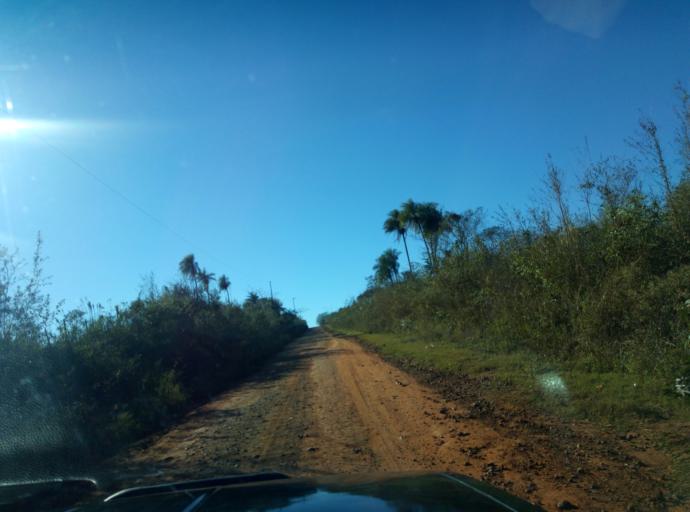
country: PY
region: Caaguazu
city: Carayao
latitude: -25.1577
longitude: -56.2968
